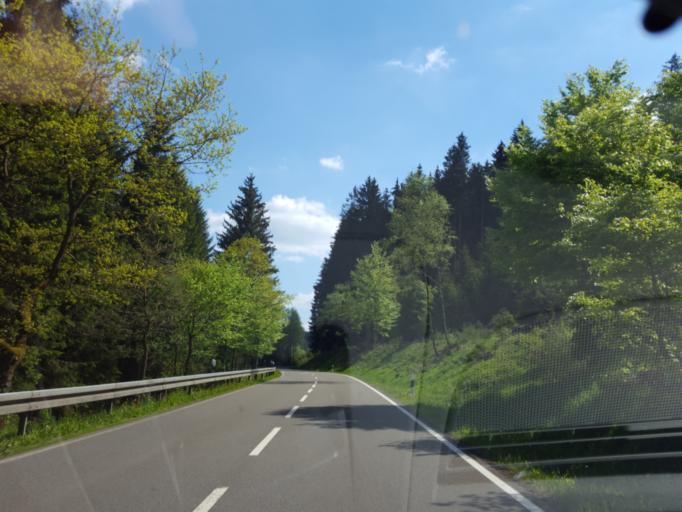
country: DE
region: North Rhine-Westphalia
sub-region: Regierungsbezirk Arnsberg
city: Olsberg
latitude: 51.2998
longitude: 8.4465
